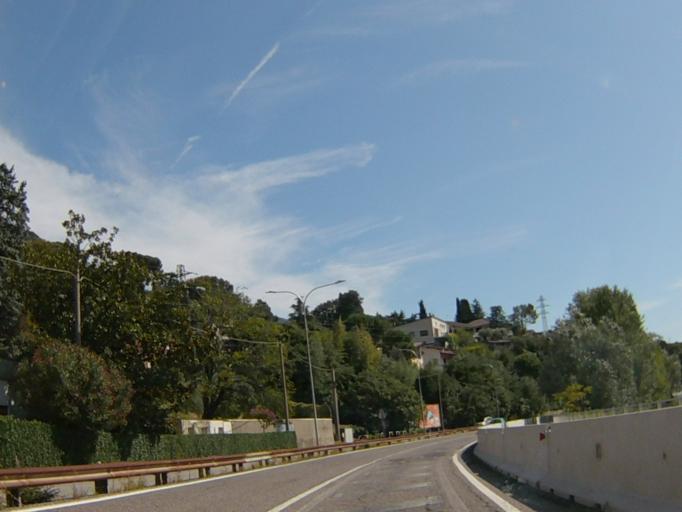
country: IT
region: Lombardy
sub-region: Provincia di Lecco
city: Lecco
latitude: 45.8665
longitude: 9.3811
